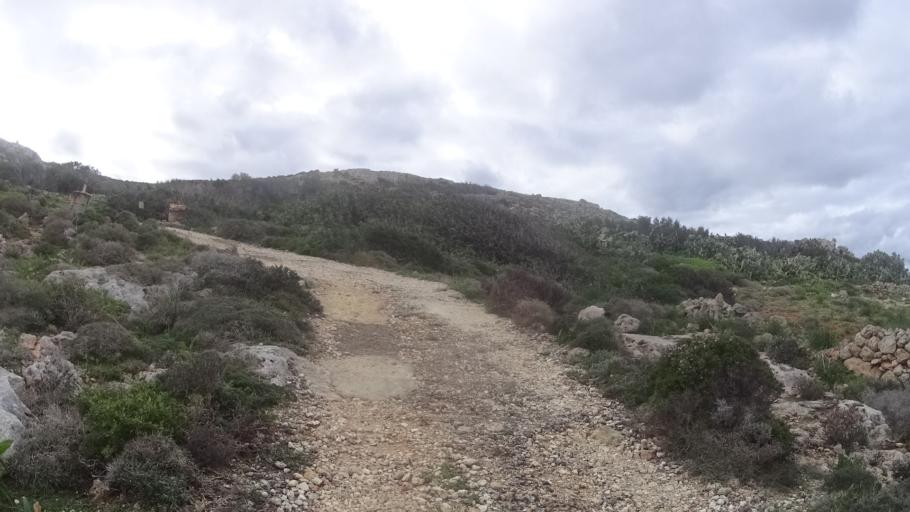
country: MT
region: Il-Mellieha
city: Mellieha
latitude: 35.9764
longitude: 14.3267
